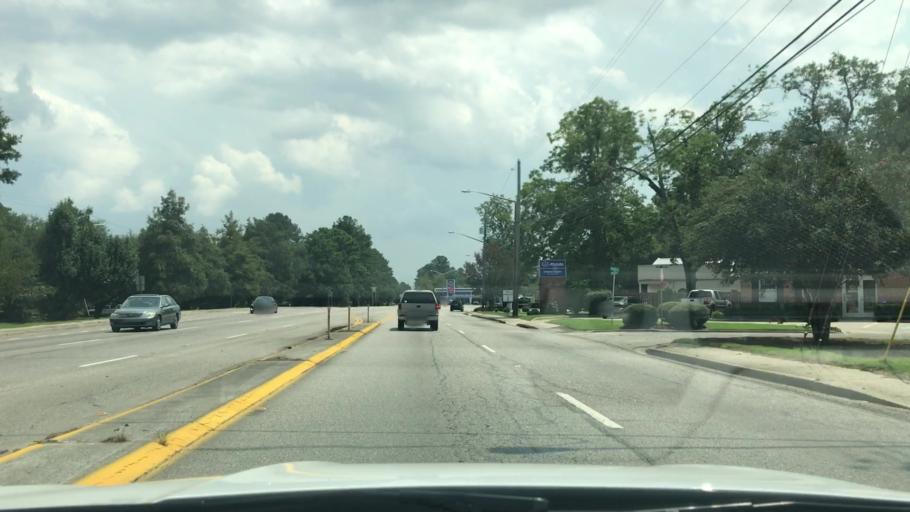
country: US
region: South Carolina
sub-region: Georgetown County
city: Georgetown
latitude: 33.3850
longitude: -79.2880
